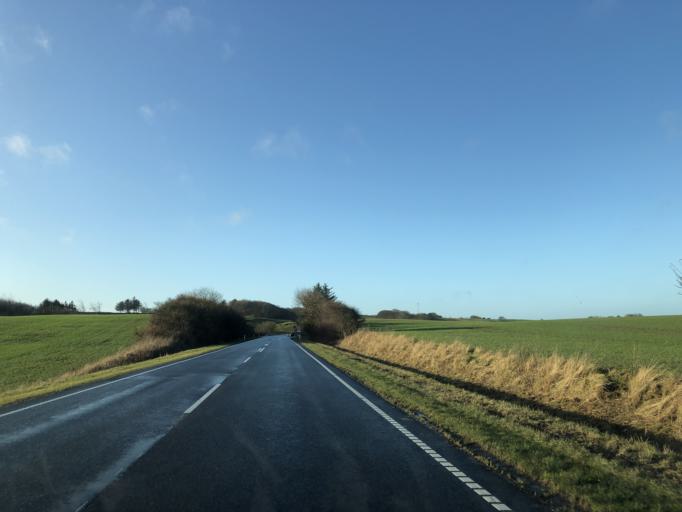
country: DK
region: Central Jutland
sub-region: Lemvig Kommune
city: Lemvig
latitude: 56.5586
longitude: 8.4451
